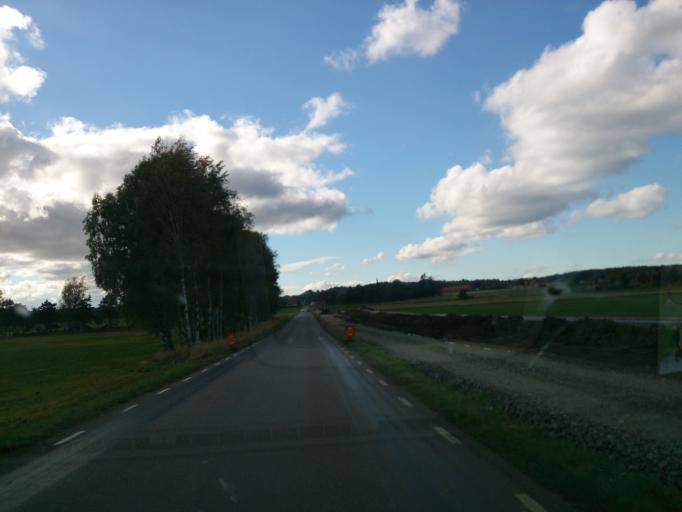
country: SE
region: Skane
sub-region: Sjobo Kommun
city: Blentarp
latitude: 55.5843
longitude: 13.6202
